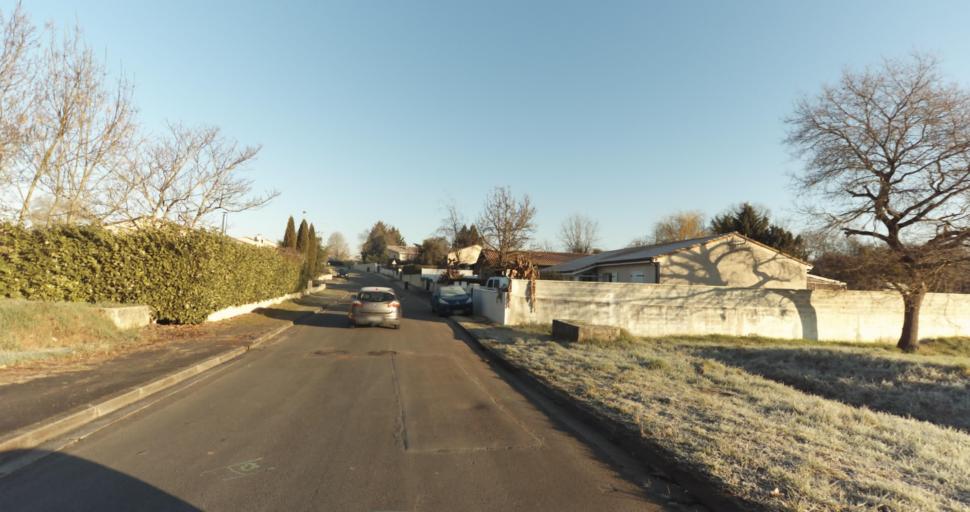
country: FR
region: Aquitaine
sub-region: Departement de la Gironde
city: Carbon-Blanc
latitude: 44.9012
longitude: -0.4991
